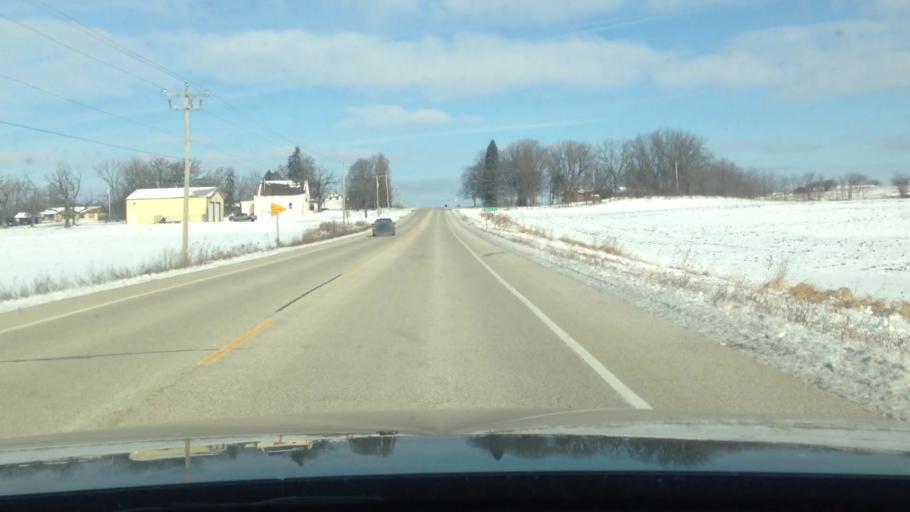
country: US
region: Wisconsin
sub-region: Walworth County
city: East Troy
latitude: 42.7105
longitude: -88.4052
